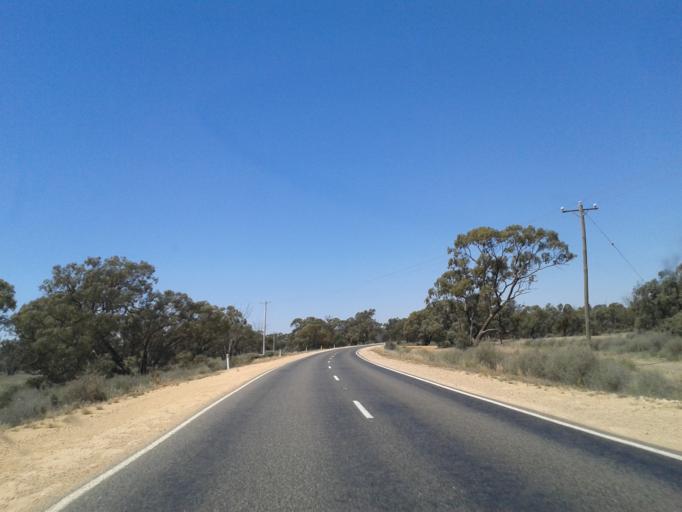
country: AU
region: Victoria
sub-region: Swan Hill
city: Swan Hill
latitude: -34.7064
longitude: 143.0785
